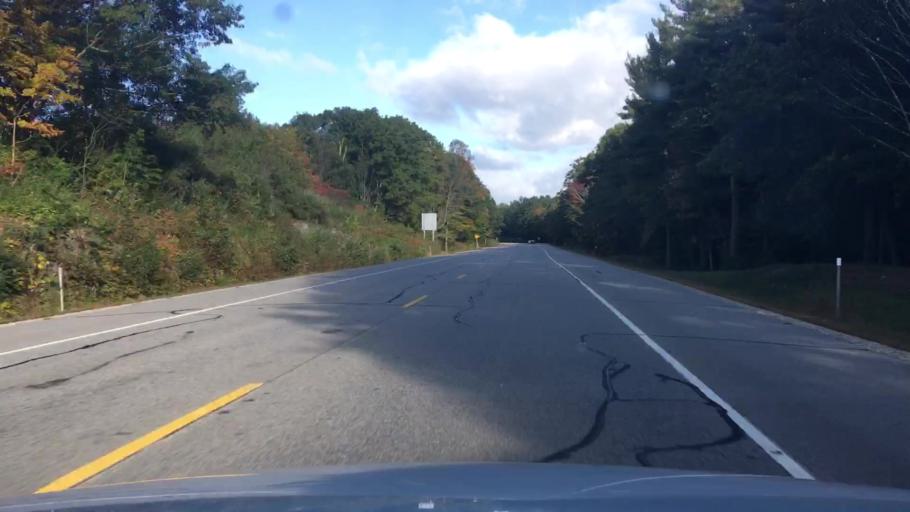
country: US
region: New Hampshire
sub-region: Strafford County
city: Durham
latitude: 43.1468
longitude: -70.9207
